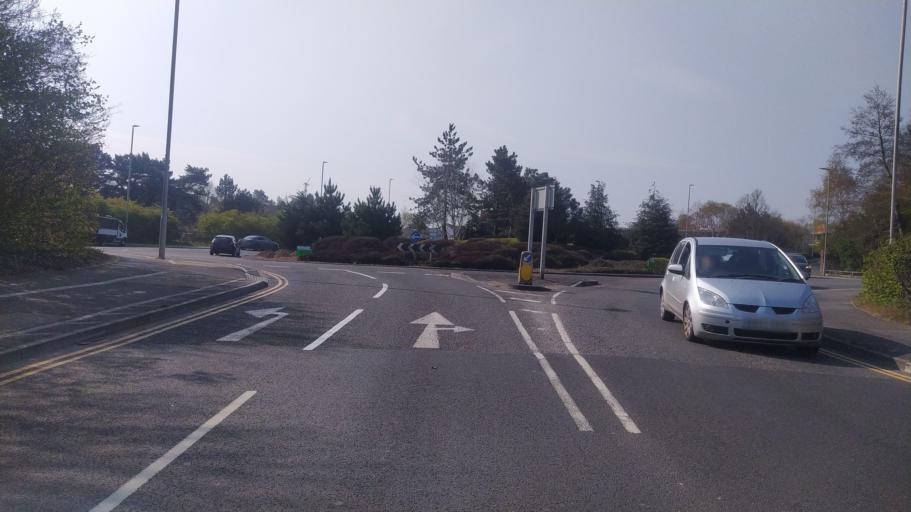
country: GB
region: England
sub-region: Dorset
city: Parkstone
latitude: 50.7413
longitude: -1.9119
